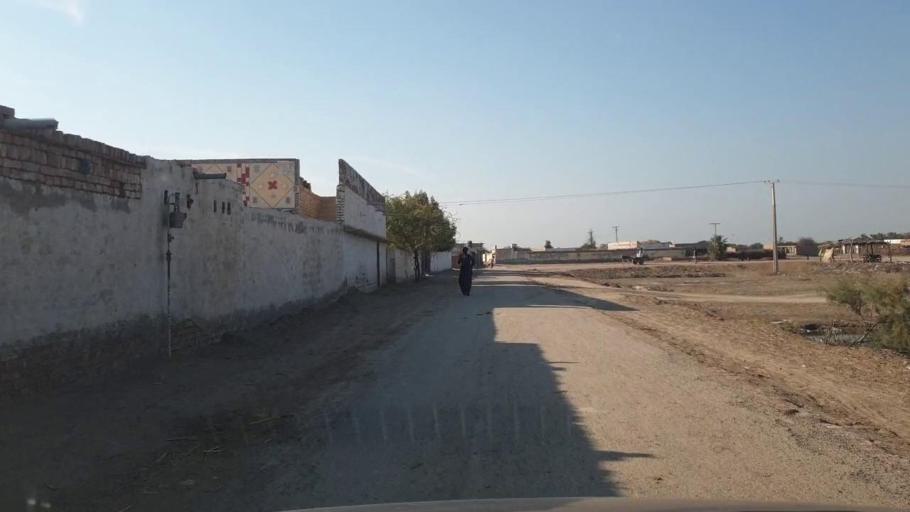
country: PK
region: Sindh
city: Shahpur Chakar
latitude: 26.1793
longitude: 68.6636
